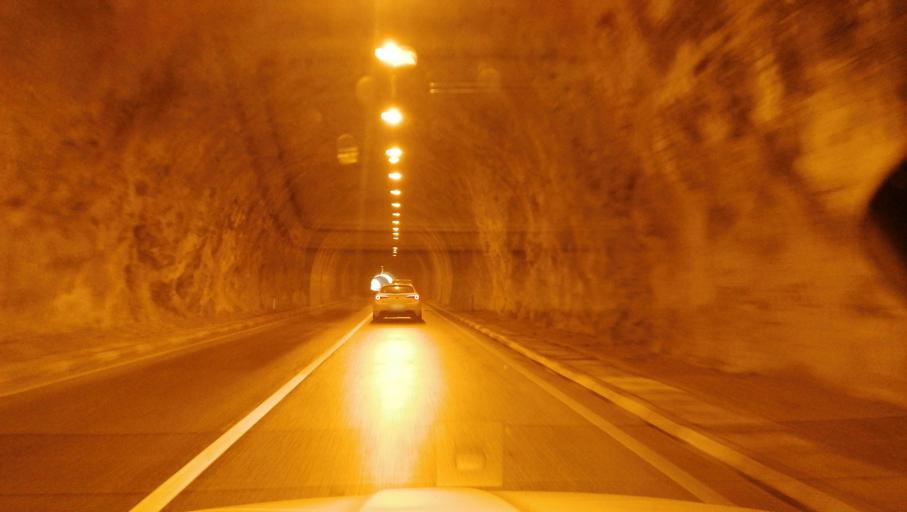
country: BA
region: Republika Srpska
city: Visegrad
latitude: 43.7376
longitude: 19.2045
